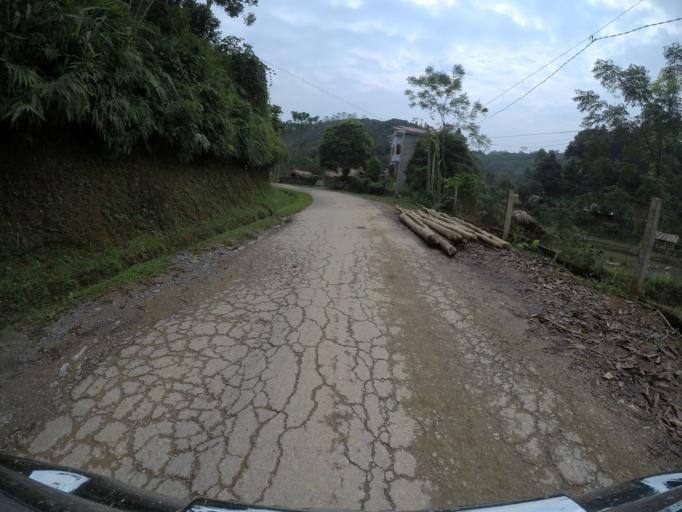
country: VN
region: Yen Bai
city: Co Phuc
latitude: 21.8217
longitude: 104.6231
